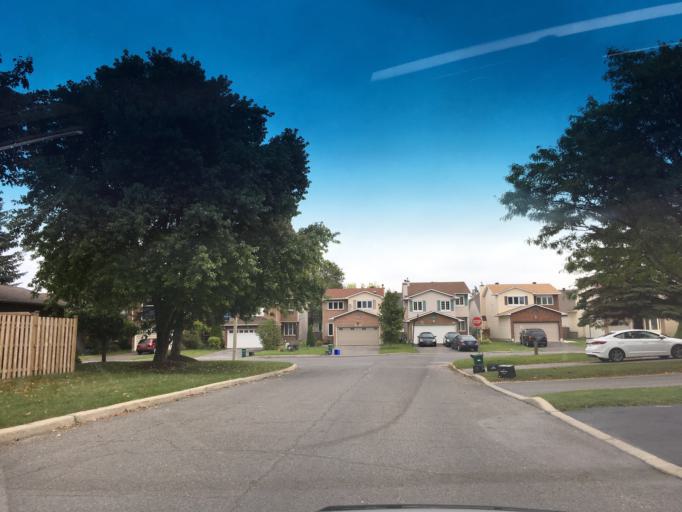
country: CA
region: Quebec
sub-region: Outaouais
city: Gatineau
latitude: 45.4571
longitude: -75.5020
